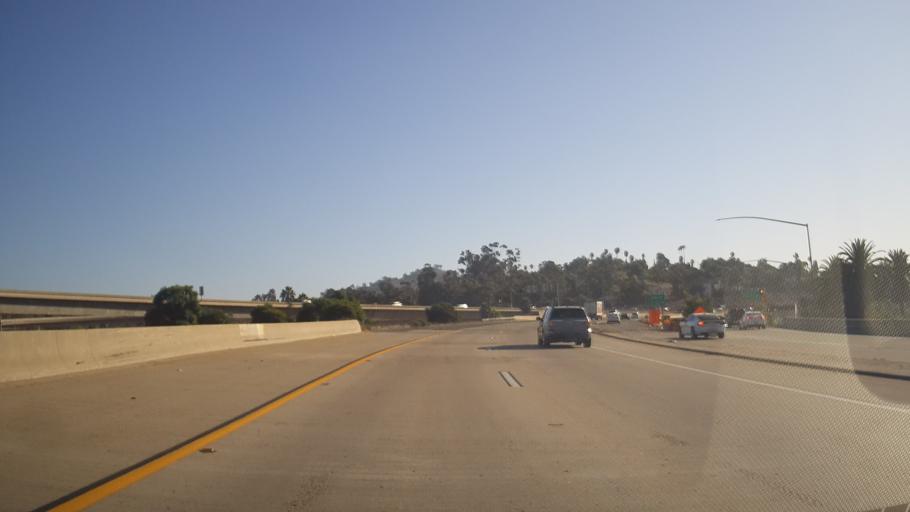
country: US
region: California
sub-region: San Diego County
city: Spring Valley
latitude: 32.7523
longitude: -117.0090
